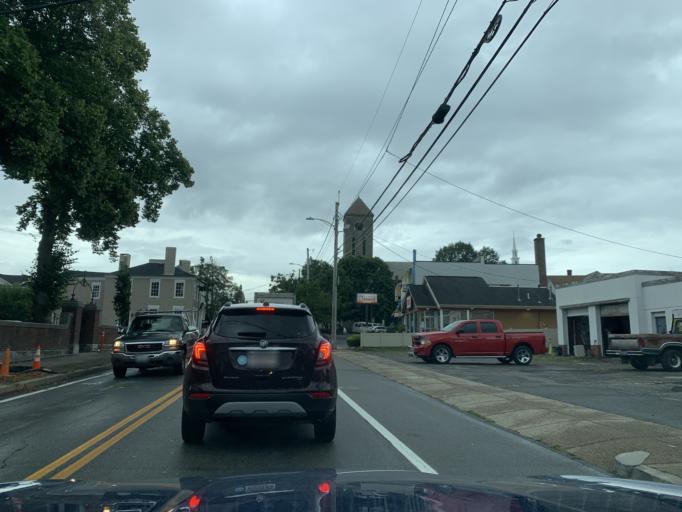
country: US
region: Rhode Island
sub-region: Bristol County
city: Warren
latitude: 41.7319
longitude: -71.2829
